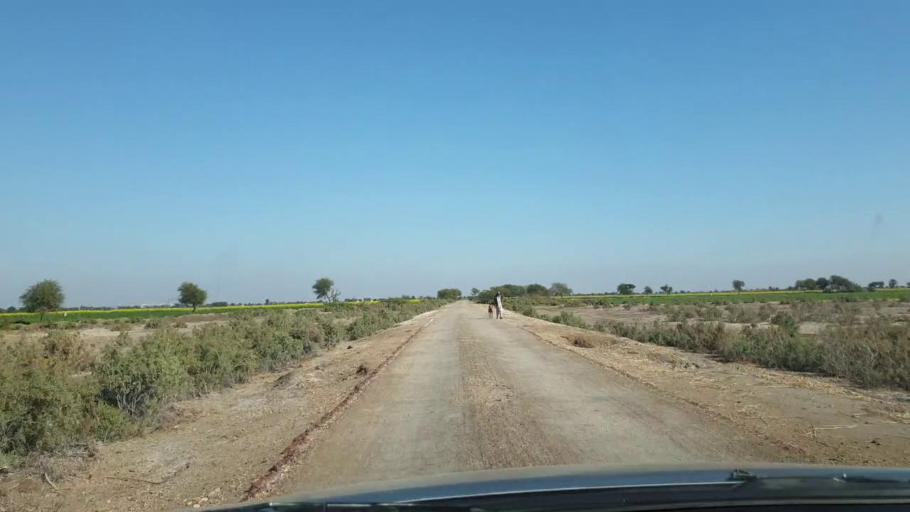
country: PK
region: Sindh
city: Jhol
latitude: 25.9165
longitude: 68.9785
